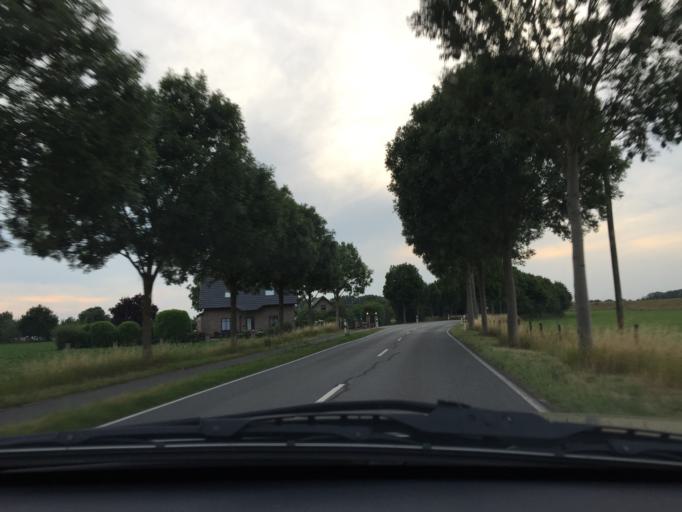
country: DE
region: North Rhine-Westphalia
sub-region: Regierungsbezirk Dusseldorf
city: Kleve
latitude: 51.7866
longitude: 6.2035
